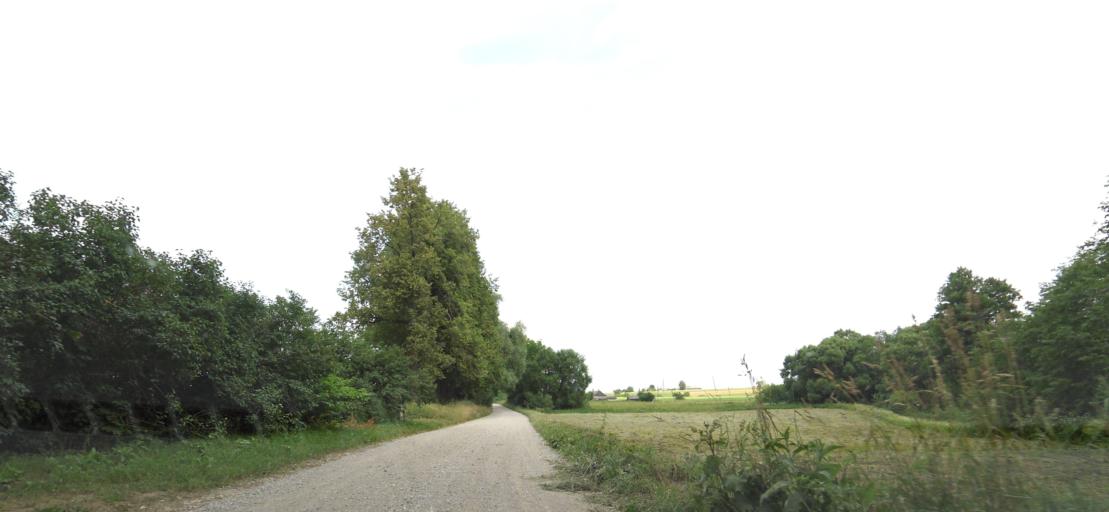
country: LT
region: Panevezys
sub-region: Birzai
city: Birzai
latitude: 56.3665
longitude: 24.7528
